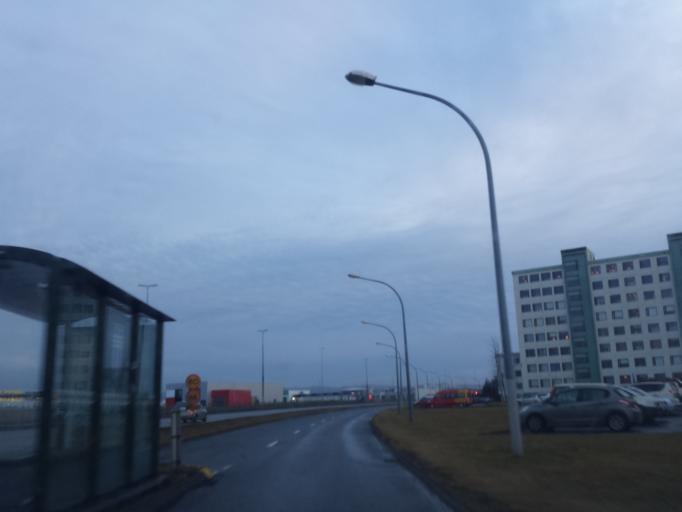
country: IS
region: Capital Region
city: Reykjavik
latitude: 64.1431
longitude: -21.8526
